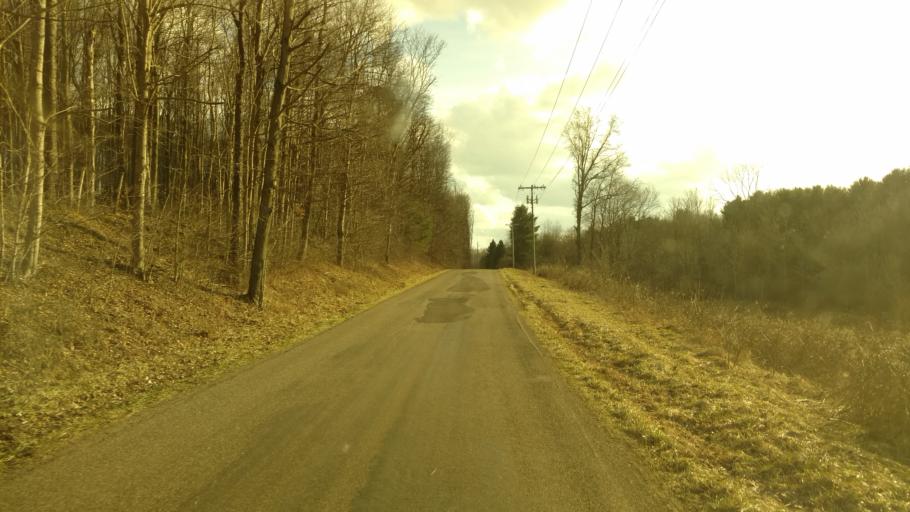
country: US
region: Ohio
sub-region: Sandusky County
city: Bellville
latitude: 40.5587
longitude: -82.4499
